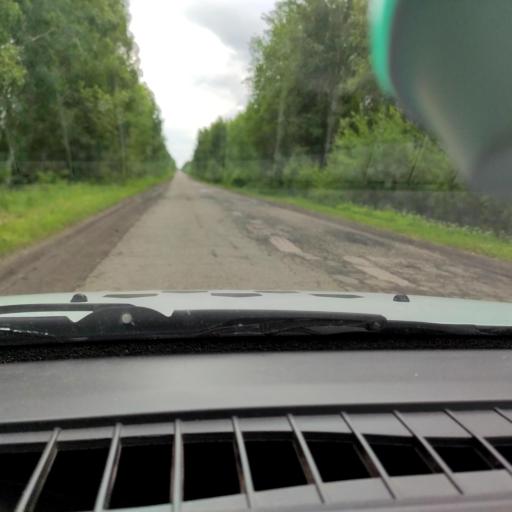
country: RU
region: Perm
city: Kukushtan
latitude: 57.2788
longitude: 56.5354
